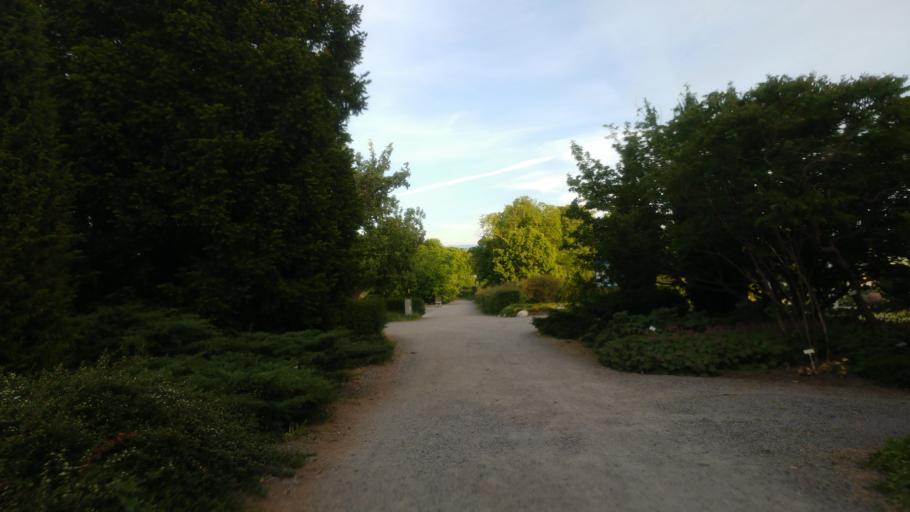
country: SE
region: Stockholm
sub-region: Norrtalje Kommun
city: Bergshamra
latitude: 59.3708
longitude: 18.0472
